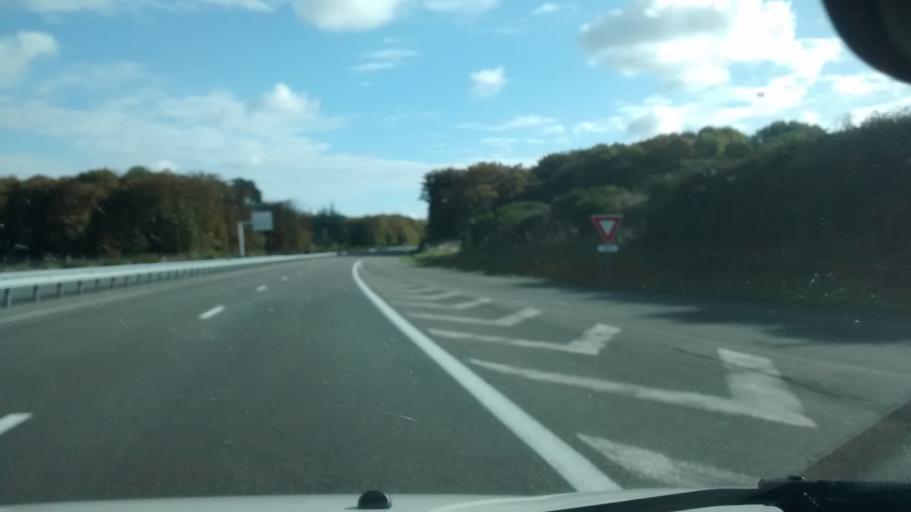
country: FR
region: Pays de la Loire
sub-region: Departement de Maine-et-Loire
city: Combree
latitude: 47.7308
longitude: -1.0727
